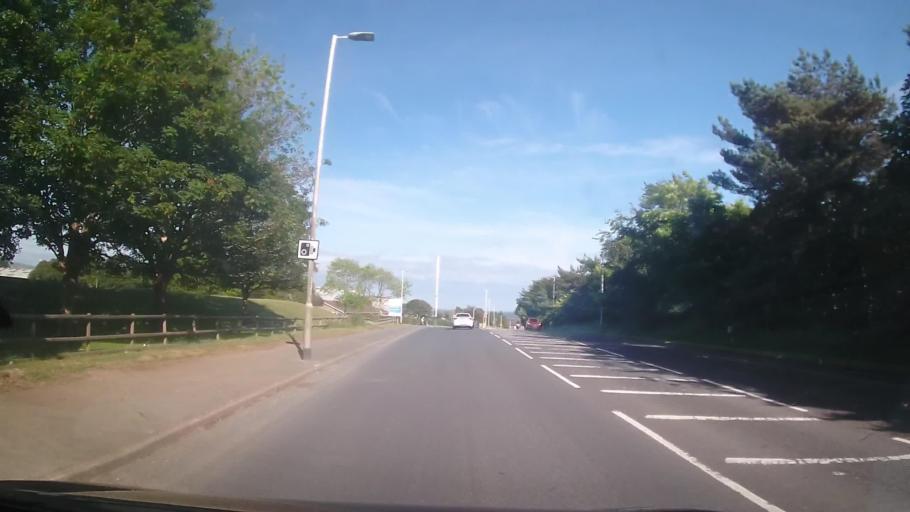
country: GB
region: England
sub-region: Devon
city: Plympton
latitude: 50.4218
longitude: -4.0987
